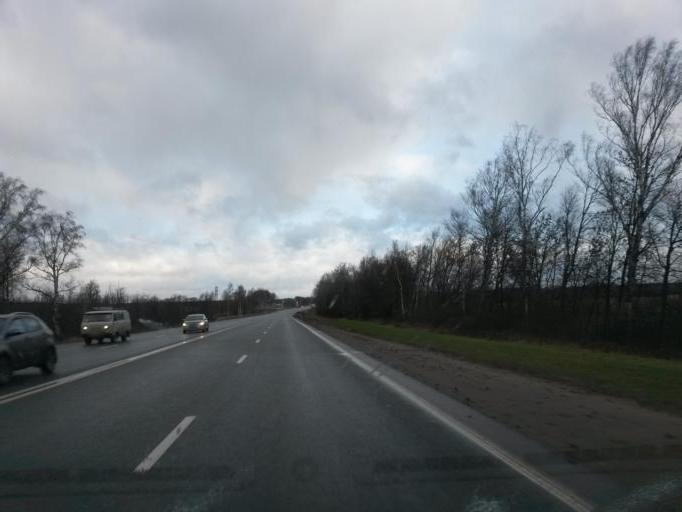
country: RU
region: Jaroslavl
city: Petrovsk
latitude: 57.0398
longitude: 39.2881
